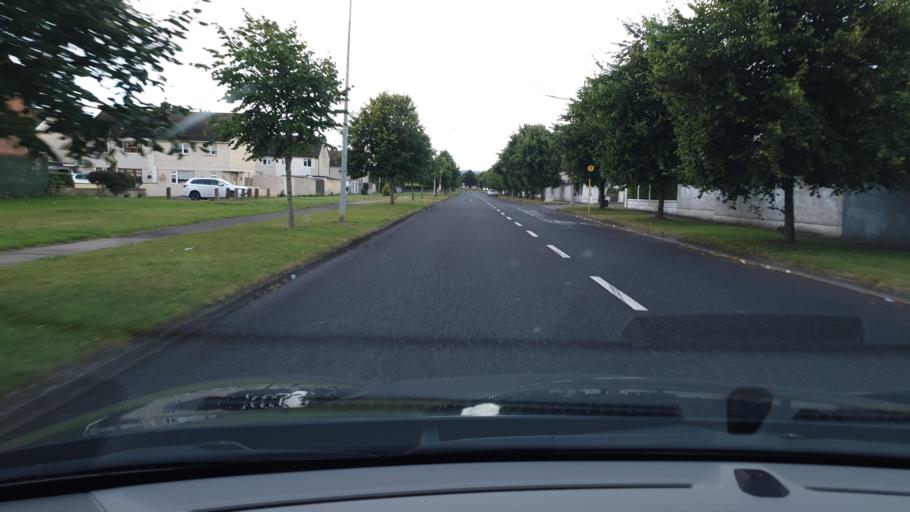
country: IE
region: Leinster
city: Clondalkin
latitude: 53.3291
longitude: -6.4239
